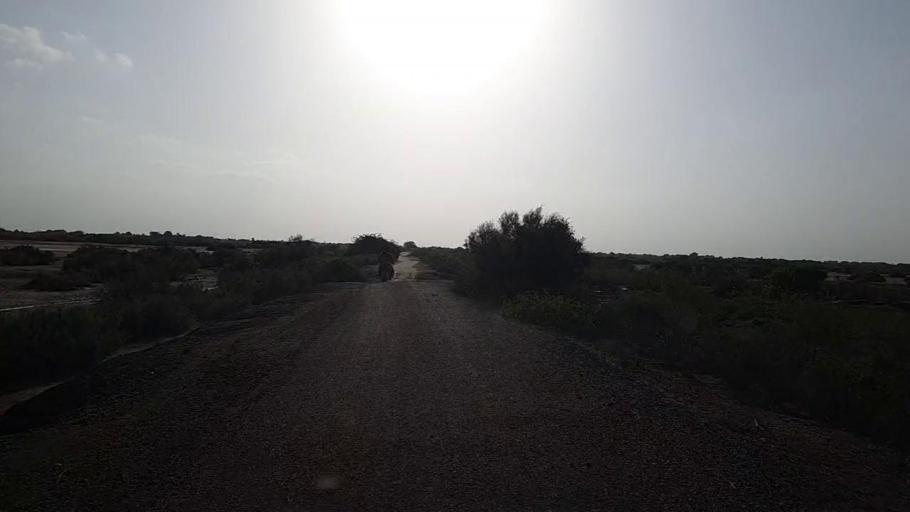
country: PK
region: Sindh
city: Mirpur Batoro
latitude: 24.6679
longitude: 68.4513
